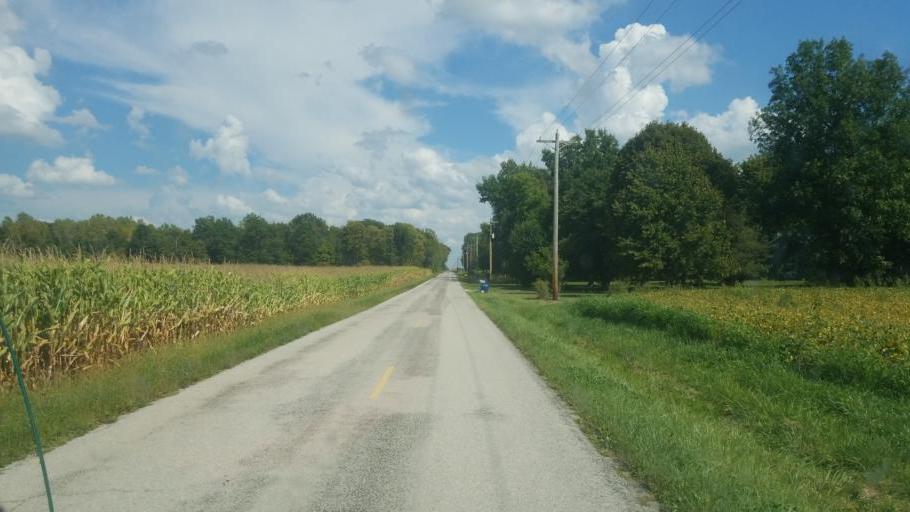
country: US
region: Ohio
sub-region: Seneca County
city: Tiffin
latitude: 40.9935
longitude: -83.1066
